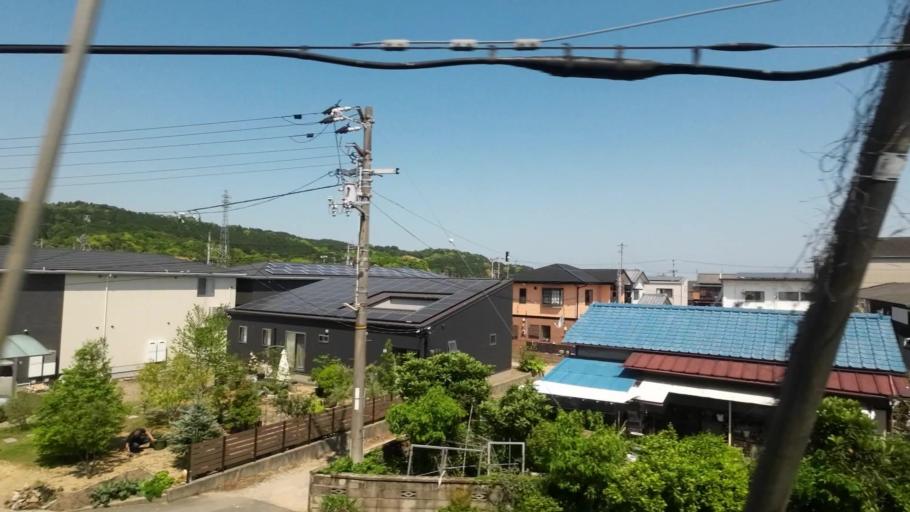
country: JP
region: Ehime
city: Niihama
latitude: 33.9410
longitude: 133.2868
